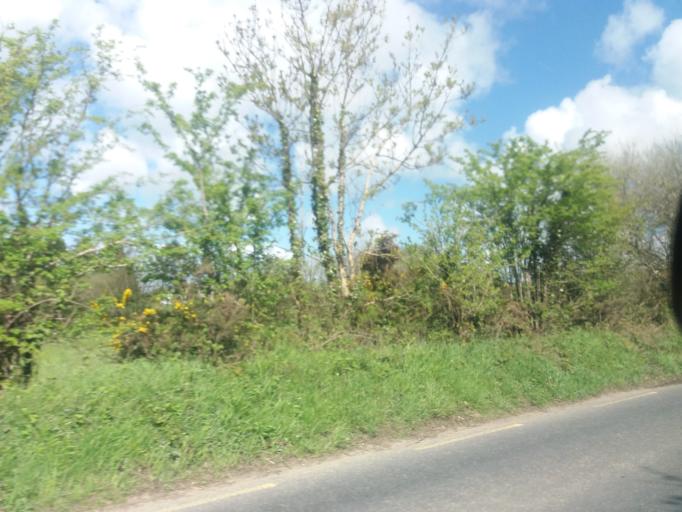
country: IE
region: Leinster
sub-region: Loch Garman
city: New Ross
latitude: 52.2756
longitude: -6.7281
